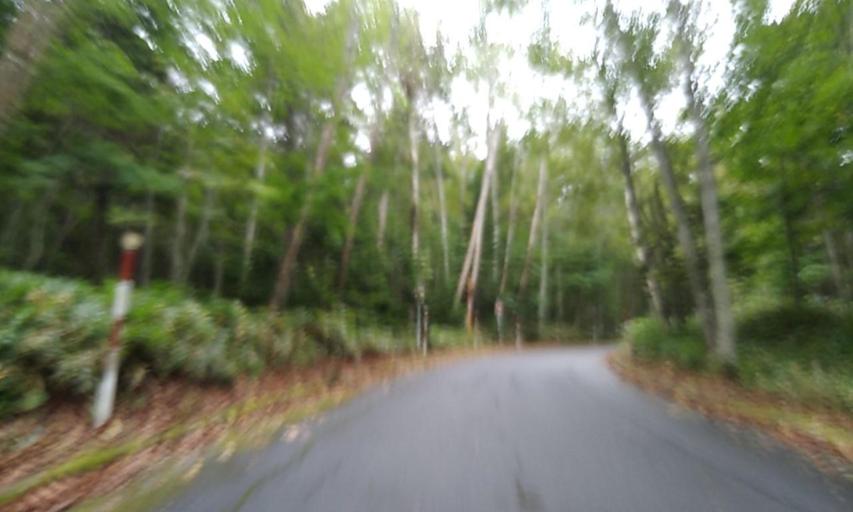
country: JP
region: Hokkaido
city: Bihoro
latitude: 43.5803
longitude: 144.2546
